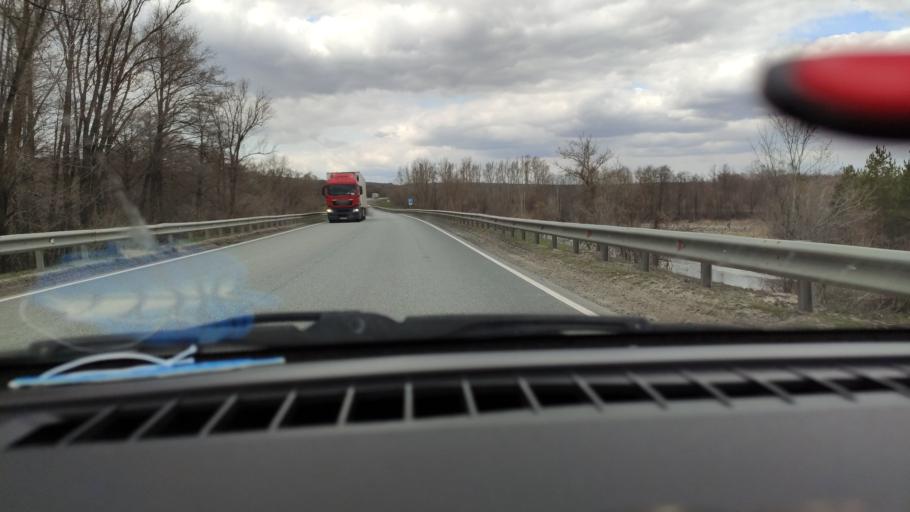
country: RU
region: Saratov
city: Tersa
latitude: 52.1024
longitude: 47.4749
